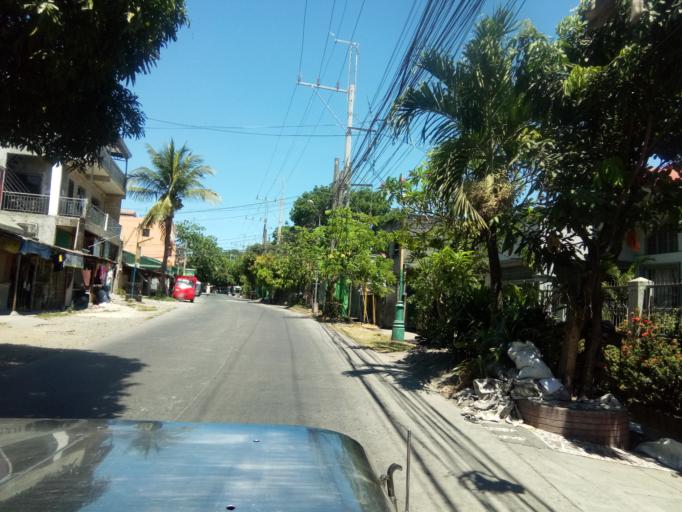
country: PH
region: Calabarzon
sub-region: Province of Cavite
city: Dasmarinas
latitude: 14.3194
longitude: 120.9696
